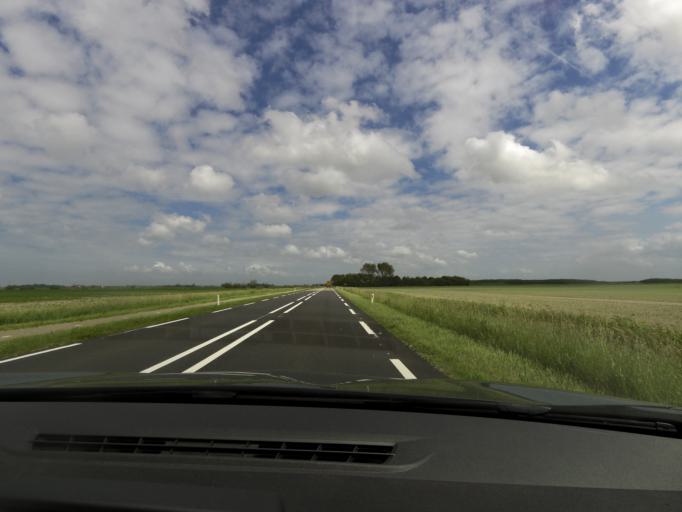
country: NL
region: Zeeland
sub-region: Schouwen-Duiveland
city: Haamstede
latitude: 51.6986
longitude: 3.7716
